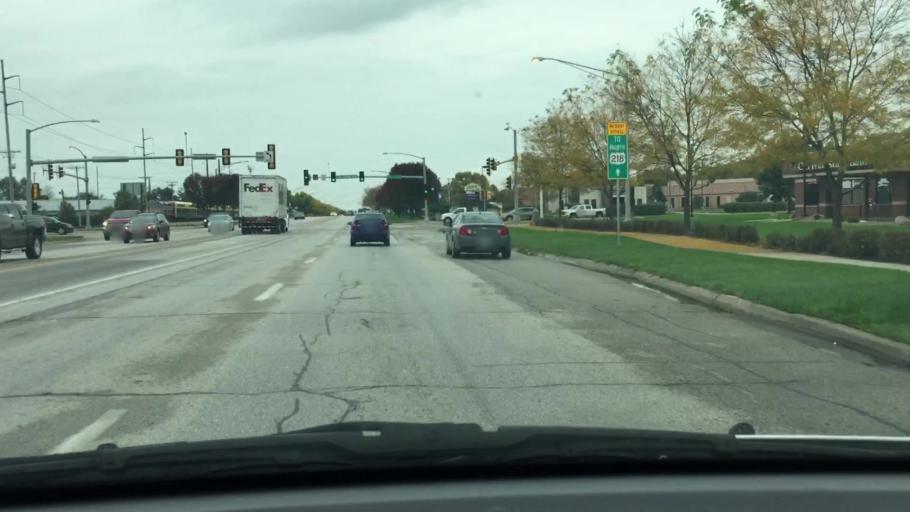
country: US
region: Iowa
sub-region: Johnson County
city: Coralville
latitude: 41.6813
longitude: -91.5949
